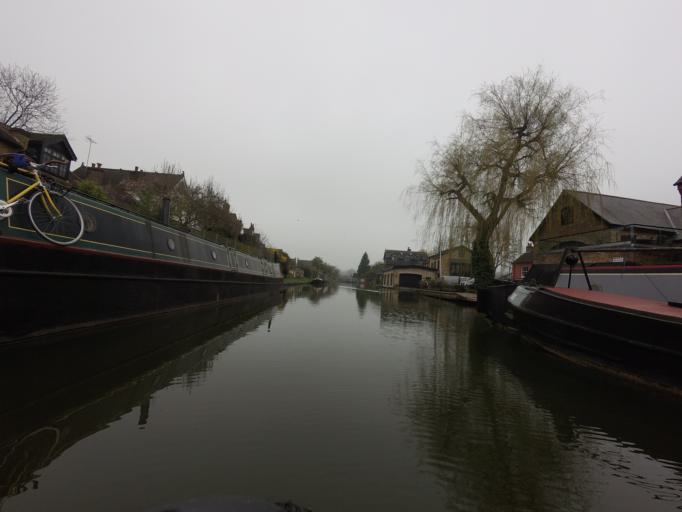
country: GB
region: England
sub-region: Hertfordshire
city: Berkhamsted
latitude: 51.7616
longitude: -0.5586
